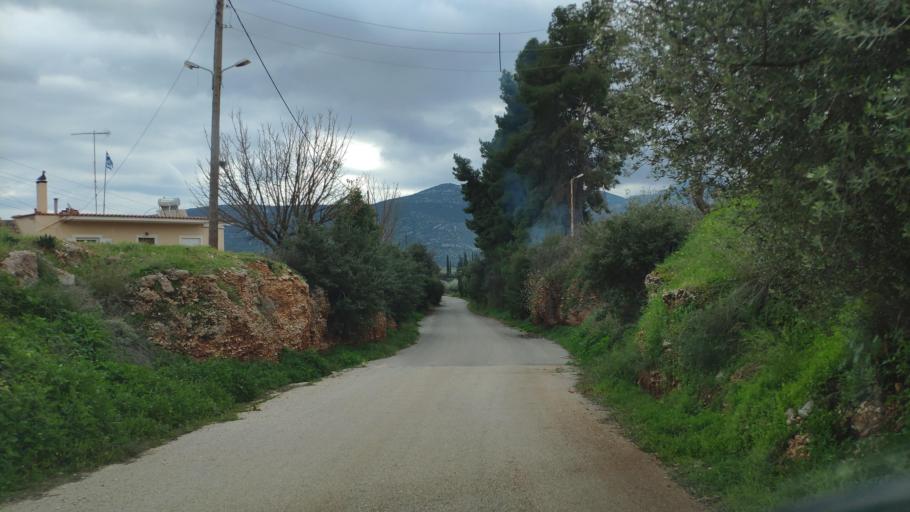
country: GR
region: Peloponnese
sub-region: Nomos Argolidos
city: Nea Kios
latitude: 37.5342
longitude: 22.6961
